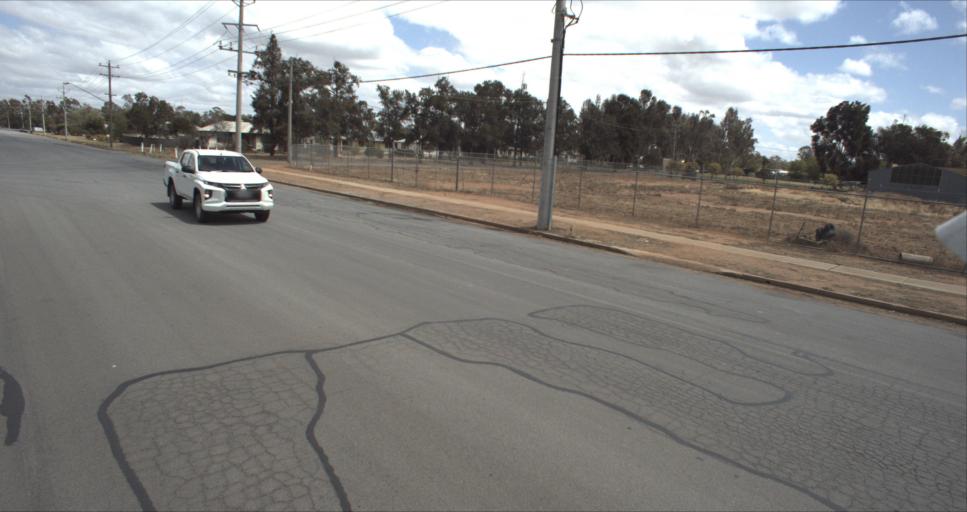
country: AU
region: New South Wales
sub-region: Leeton
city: Leeton
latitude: -34.5558
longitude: 146.3936
